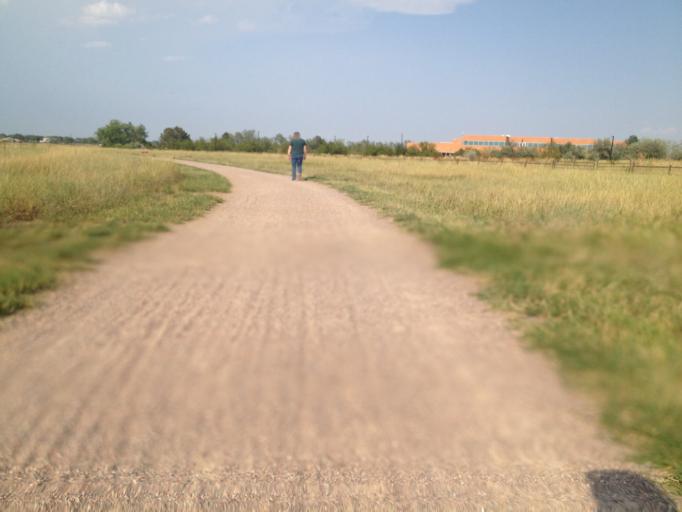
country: US
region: Colorado
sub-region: Boulder County
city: Superior
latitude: 39.9715
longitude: -105.1733
